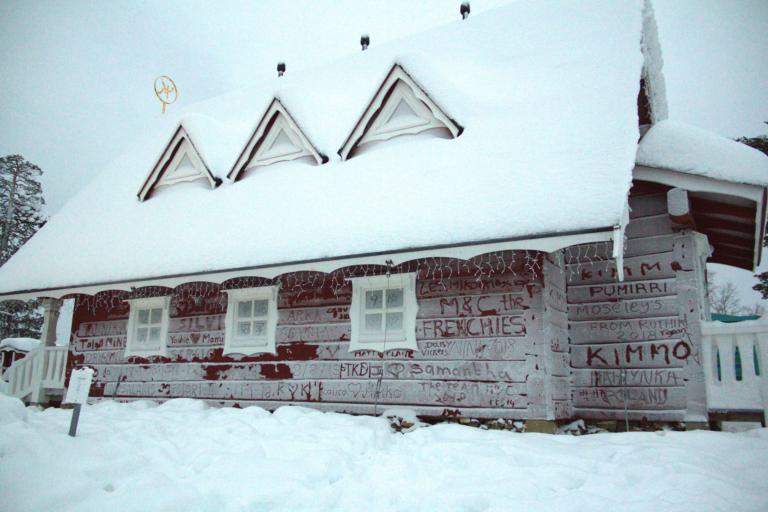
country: FI
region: Lapland
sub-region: Pohjois-Lappi
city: Ivalo
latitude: 68.4199
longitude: 27.4143
